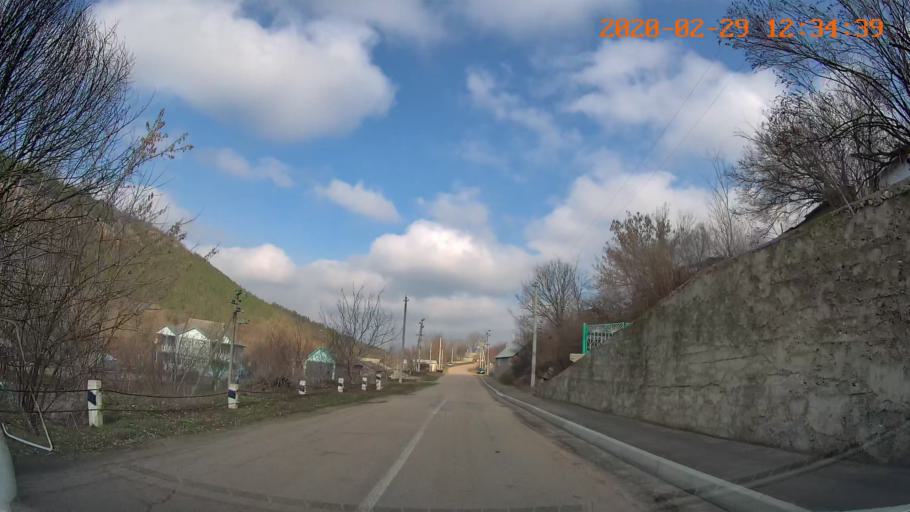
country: MD
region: Telenesti
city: Camenca
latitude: 48.0411
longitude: 28.7155
